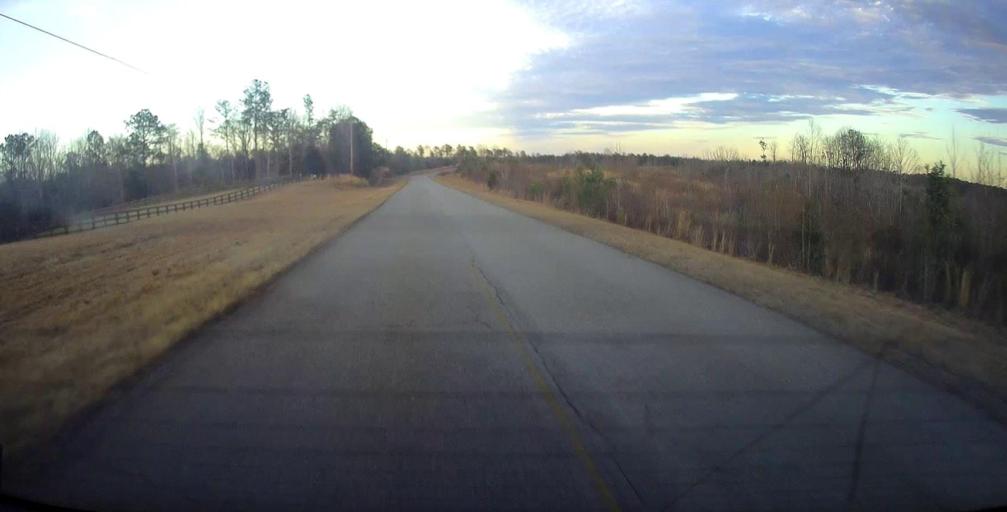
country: US
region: Georgia
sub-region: Harris County
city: Hamilton
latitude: 32.6138
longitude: -84.8360
